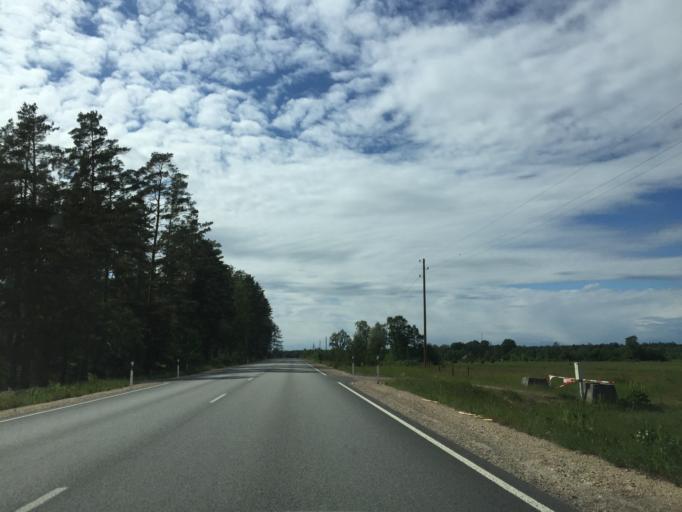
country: LV
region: Salaspils
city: Salaspils
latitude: 56.8953
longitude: 24.4403
